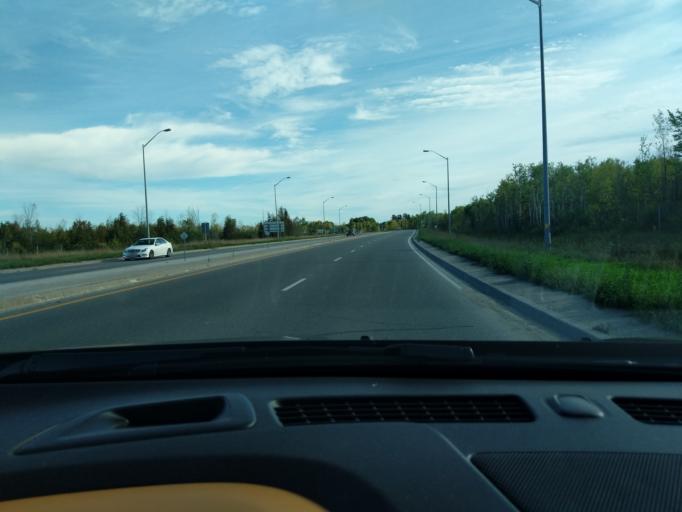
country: CA
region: Ontario
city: Collingwood
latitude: 44.4865
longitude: -80.1736
